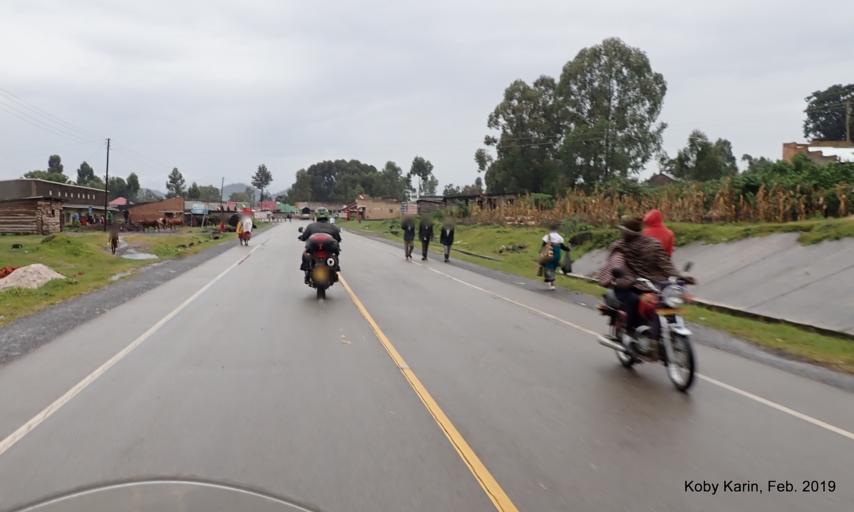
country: UG
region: Western Region
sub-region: Kisoro District
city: Kisoro
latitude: -1.3365
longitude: 29.7377
